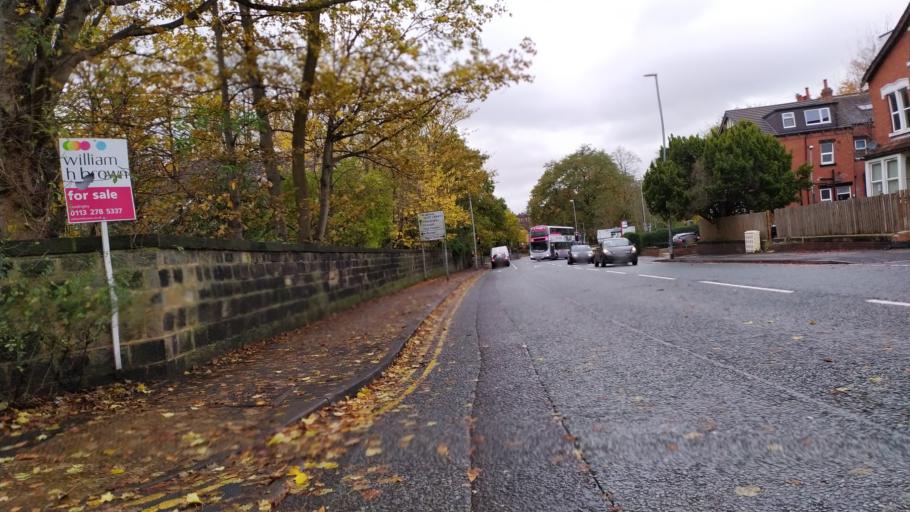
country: GB
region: England
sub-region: City and Borough of Leeds
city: Leeds
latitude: 53.8172
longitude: -1.5880
